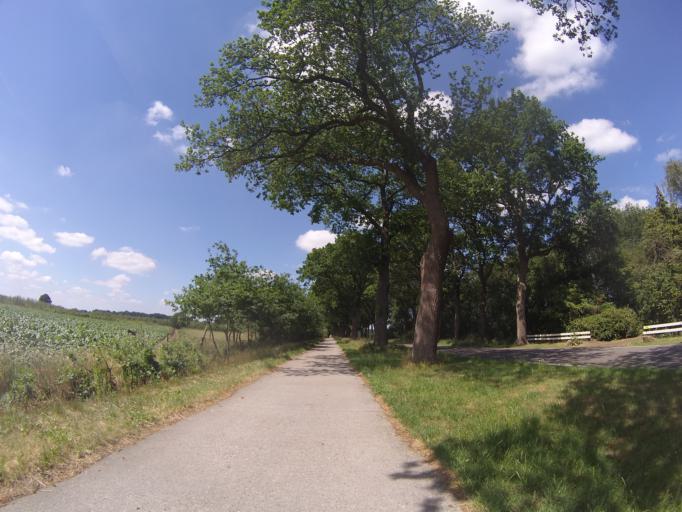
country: NL
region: Drenthe
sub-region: Gemeente Emmen
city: Emmen
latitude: 52.8452
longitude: 6.8697
